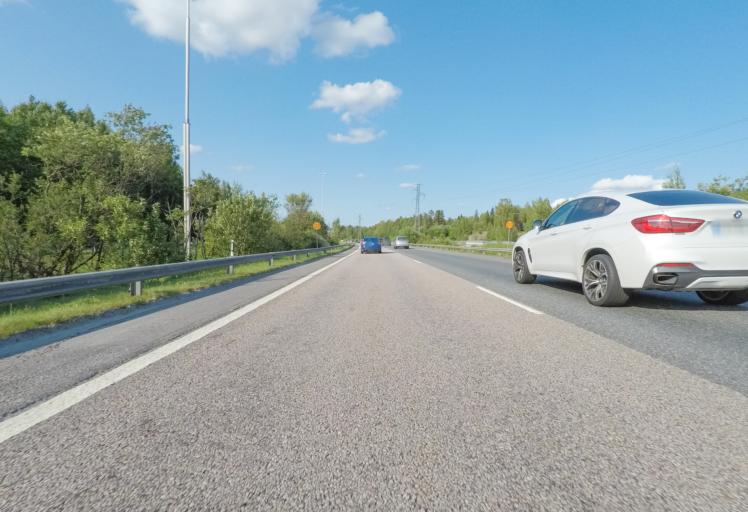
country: FI
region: Uusimaa
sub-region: Helsinki
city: Kerava
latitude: 60.3954
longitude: 25.1257
